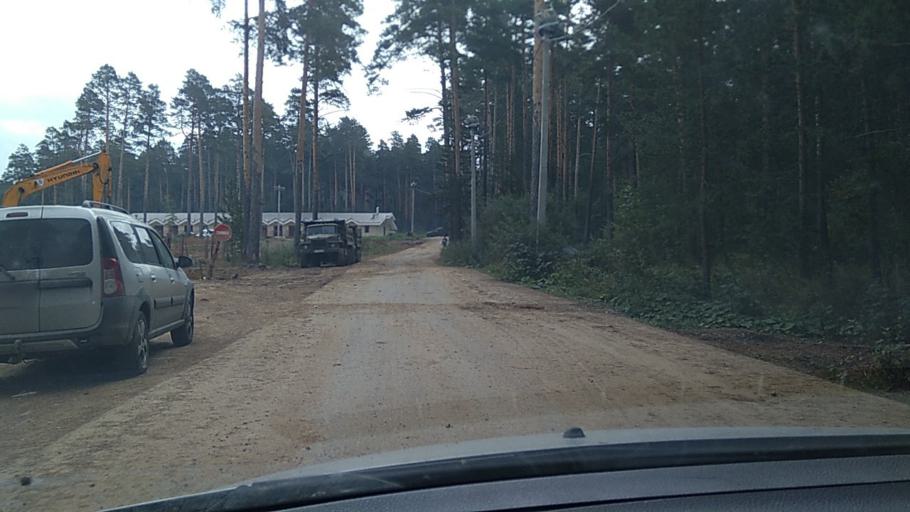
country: RU
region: Chelyabinsk
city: Zlatoust
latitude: 55.1603
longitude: 59.7007
